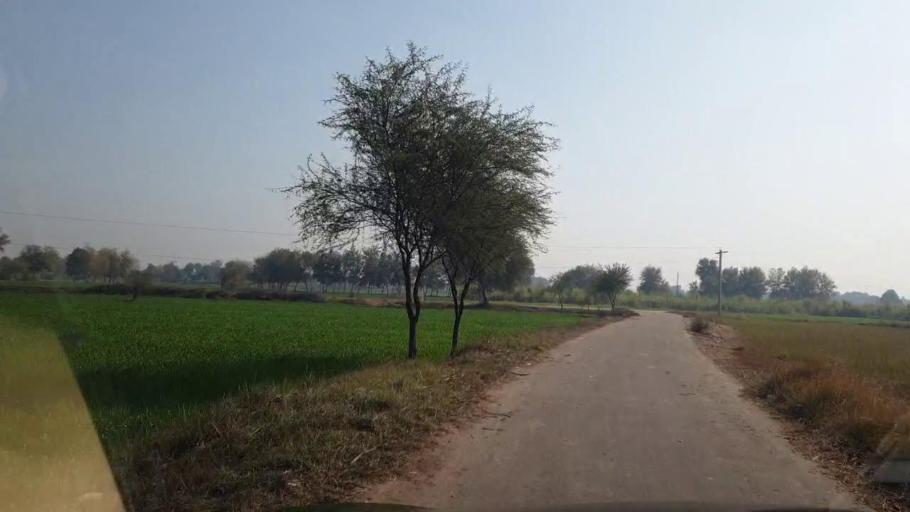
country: PK
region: Sindh
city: Ubauro
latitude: 28.1305
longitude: 69.7682
